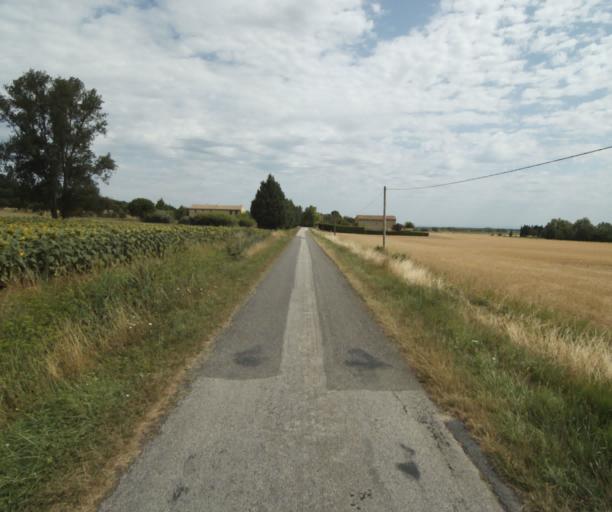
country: FR
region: Midi-Pyrenees
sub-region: Departement de la Haute-Garonne
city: Saint-Felix-Lauragais
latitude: 43.4412
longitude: 1.9067
